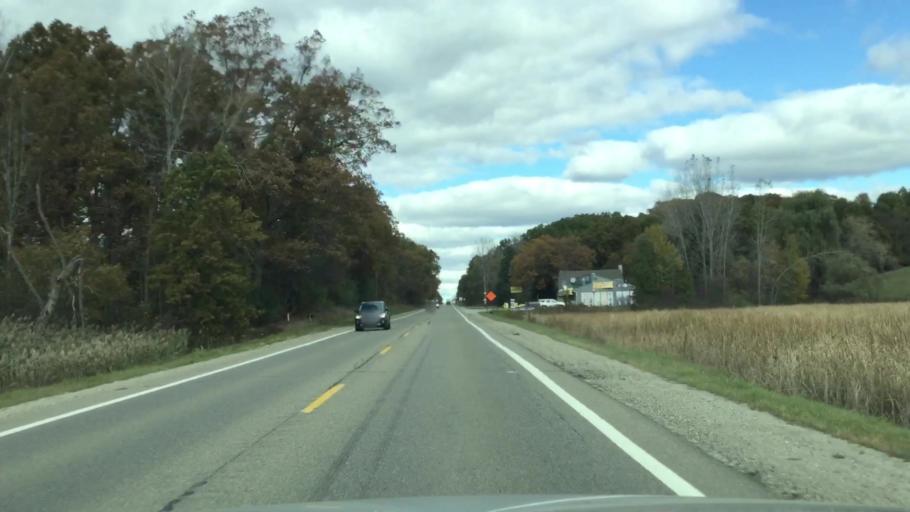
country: US
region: Michigan
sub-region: Lapeer County
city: Barnes Lake-Millers Lake
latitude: 43.1685
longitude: -83.3119
